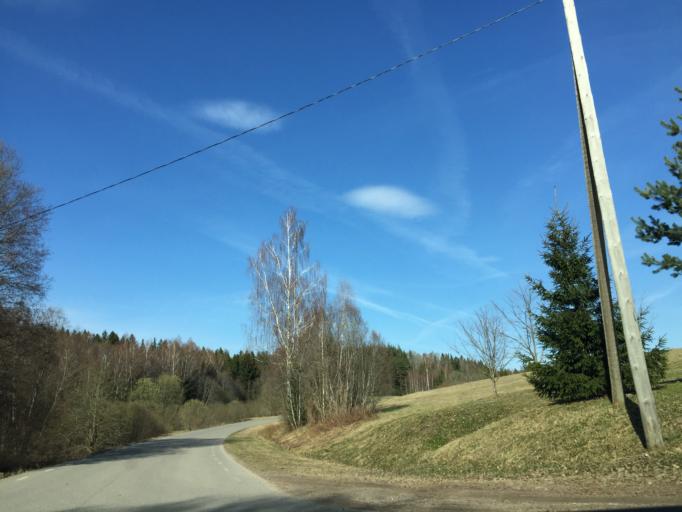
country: EE
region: Vorumaa
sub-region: Antsla vald
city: Vana-Antsla
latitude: 58.0209
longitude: 26.4673
